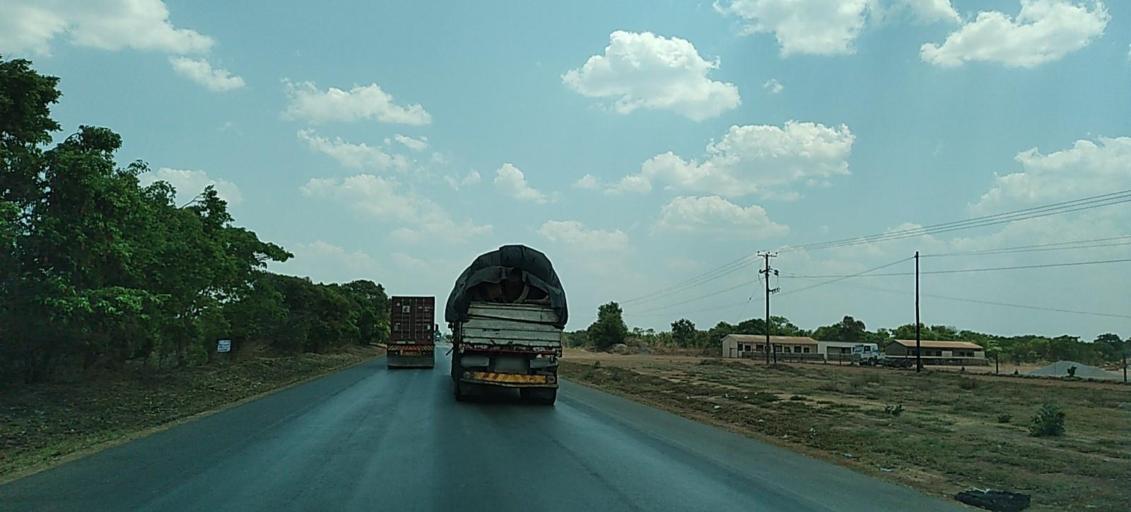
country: ZM
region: Central
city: Kabwe
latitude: -14.3669
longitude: 28.5105
